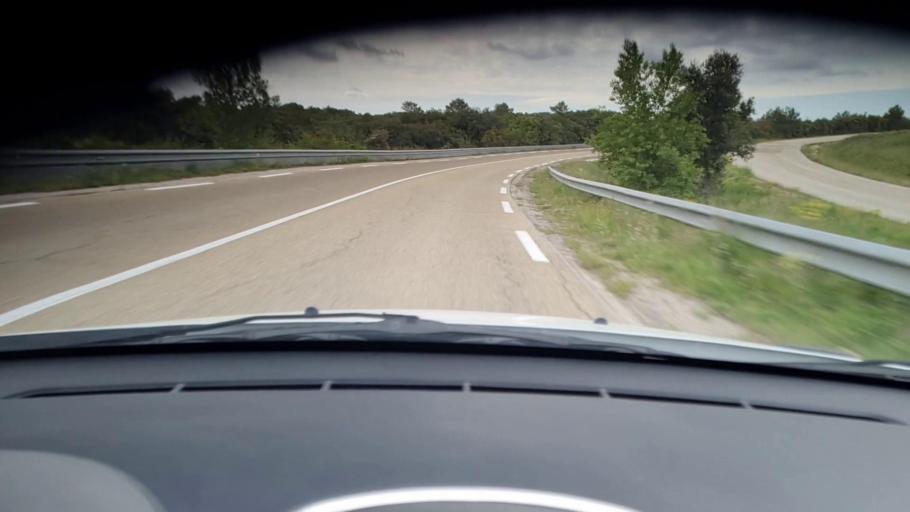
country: FR
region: Languedoc-Roussillon
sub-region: Departement du Gard
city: Poulx
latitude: 43.9026
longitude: 4.3959
